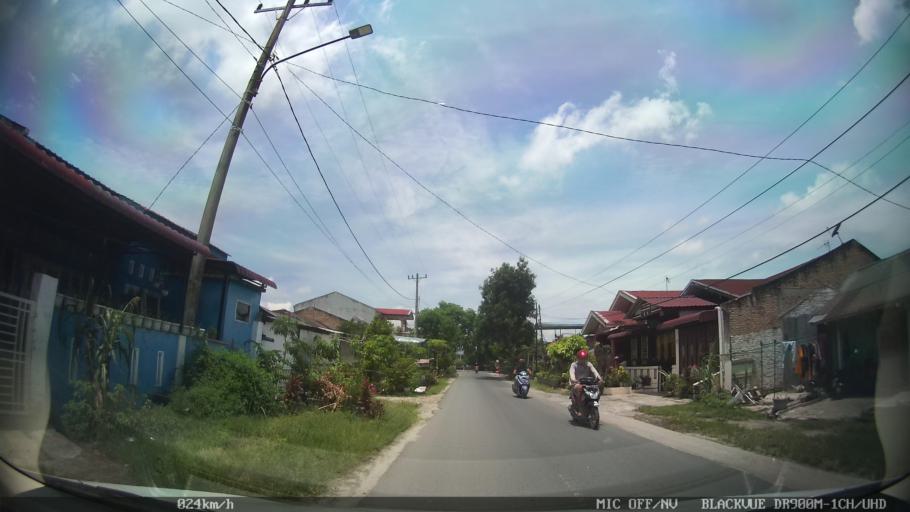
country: ID
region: North Sumatra
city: Perbaungan
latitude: 3.5427
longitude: 98.8771
